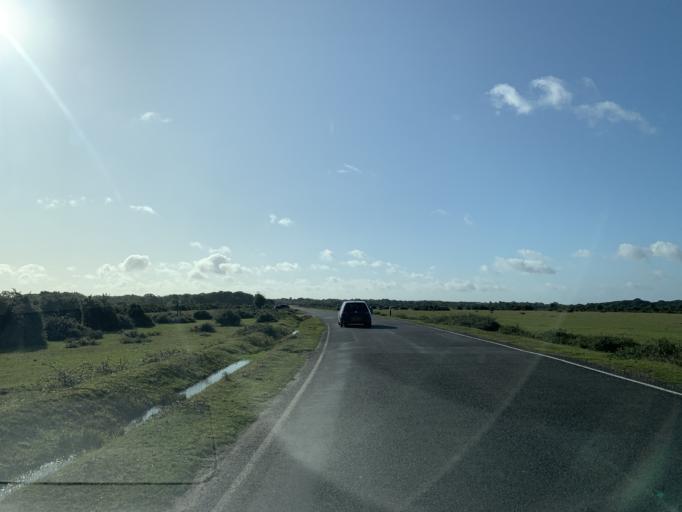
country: GB
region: England
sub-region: Hampshire
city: Cadnam
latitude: 50.9193
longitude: -1.6514
